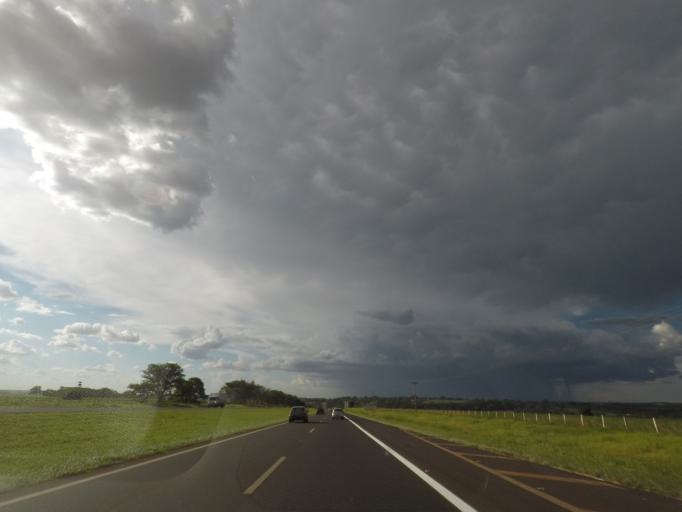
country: BR
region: Sao Paulo
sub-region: Jardinopolis
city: Jardinopolis
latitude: -21.0794
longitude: -47.8041
